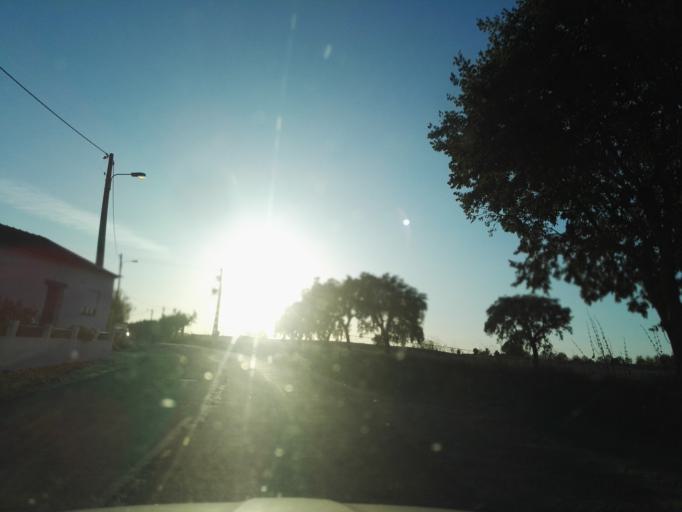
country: PT
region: Santarem
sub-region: Alpiarca
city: Alpiarca
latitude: 39.3265
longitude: -8.6161
